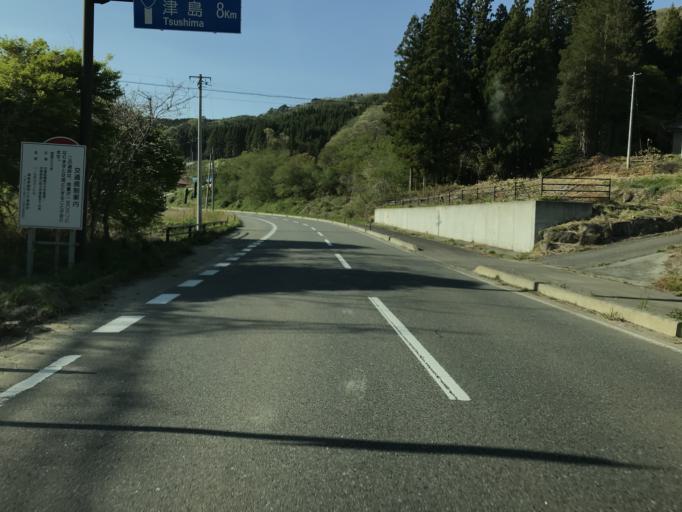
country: JP
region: Fukushima
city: Funehikimachi-funehiki
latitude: 37.5138
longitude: 140.7581
